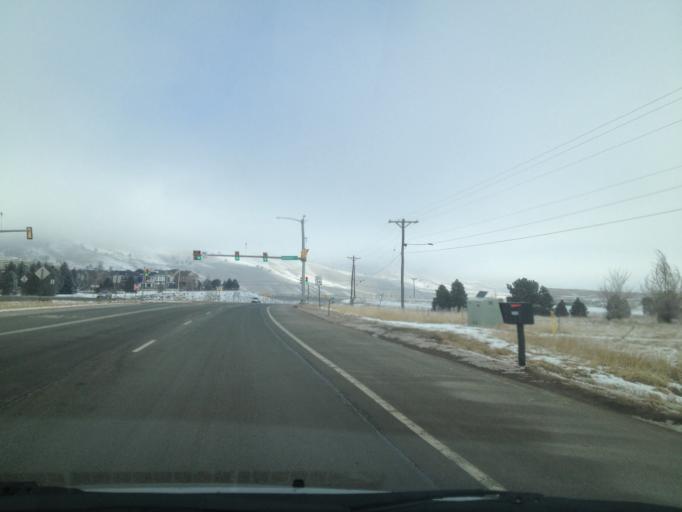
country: US
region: Colorado
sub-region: Boulder County
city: Boulder
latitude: 40.0646
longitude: -105.2809
